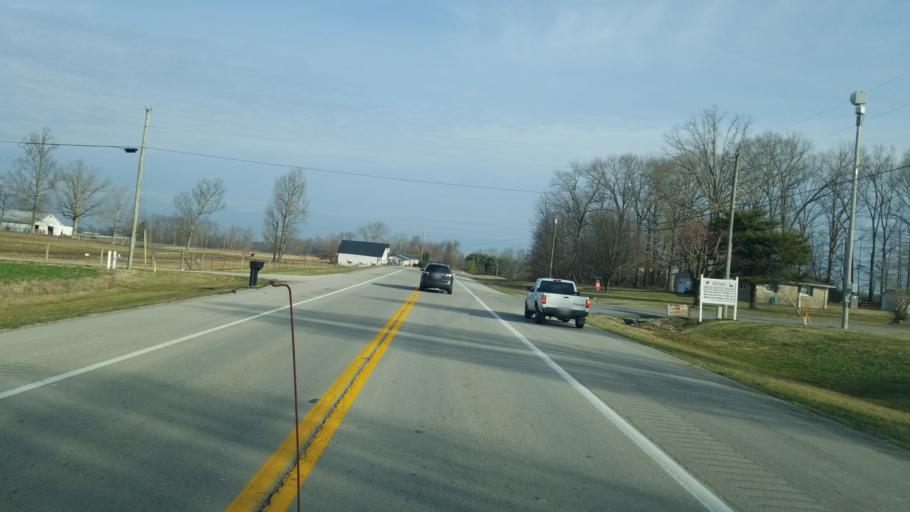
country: US
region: Kentucky
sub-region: Russell County
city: Russell Springs
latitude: 37.1418
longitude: -85.0315
